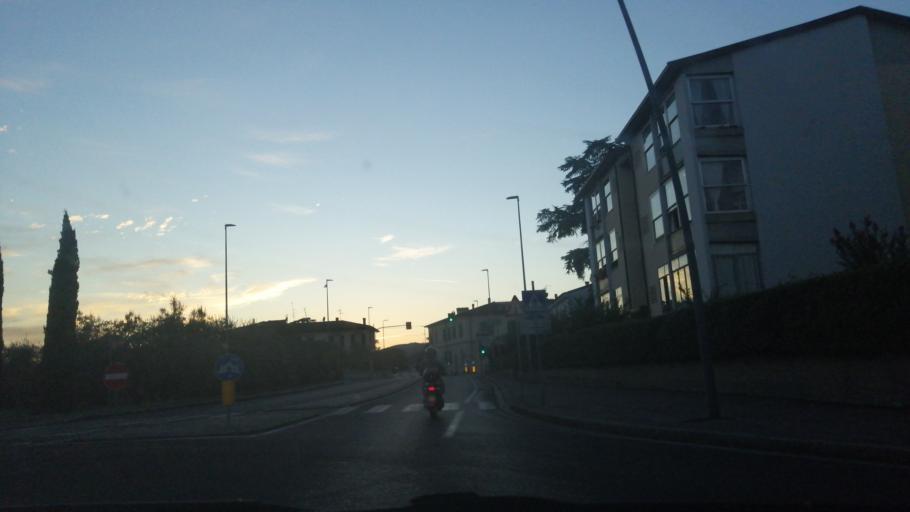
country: IT
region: Tuscany
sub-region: Province of Florence
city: Sesto Fiorentino
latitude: 43.8373
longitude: 11.2068
